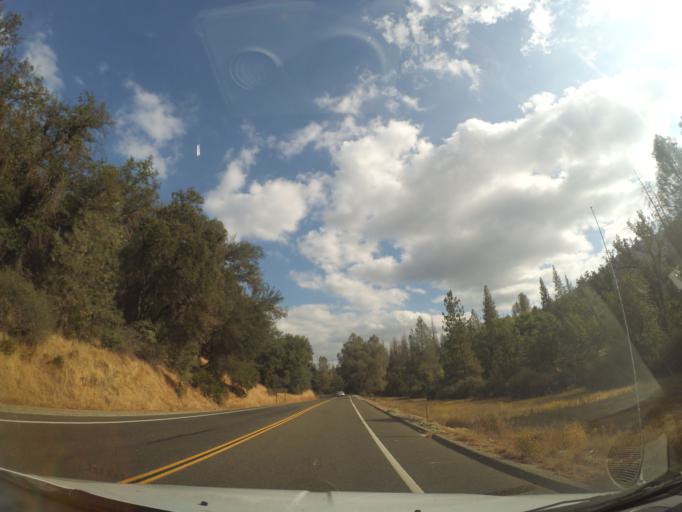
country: US
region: California
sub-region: Mariposa County
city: Midpines
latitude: 37.5636
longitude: -119.9389
